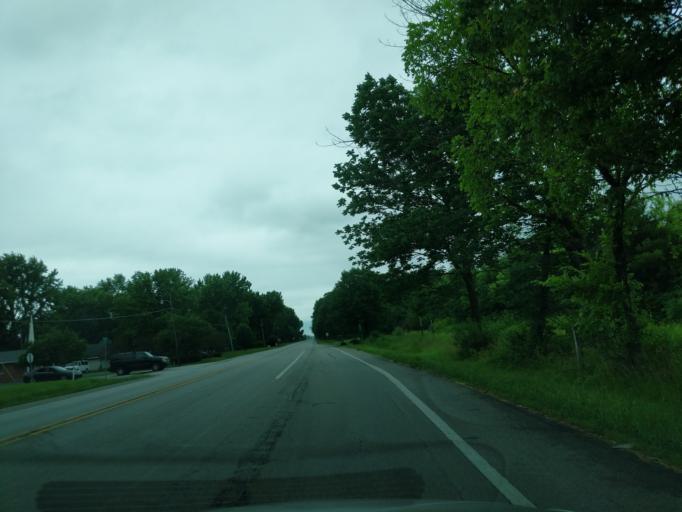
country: US
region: Indiana
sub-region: Hamilton County
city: Noblesville
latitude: 40.0724
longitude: -86.0146
